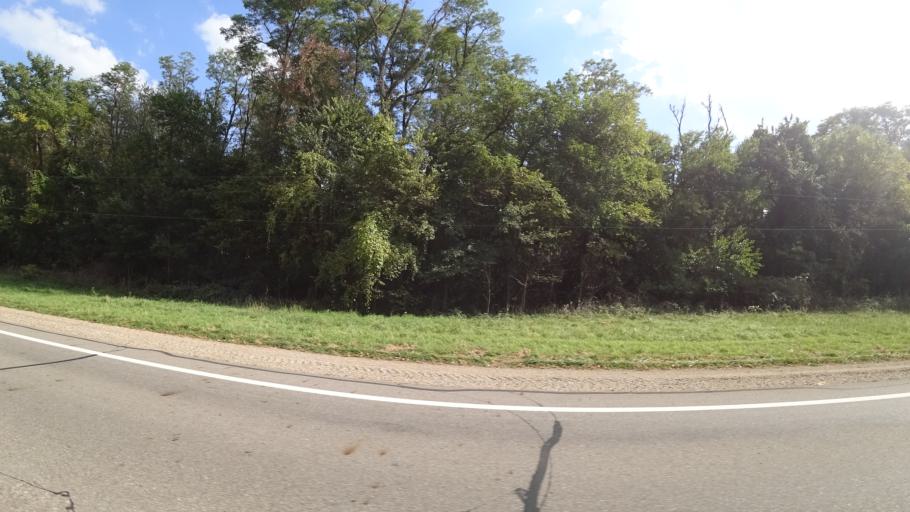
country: US
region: Michigan
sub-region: Saint Joseph County
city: Three Rivers
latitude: 41.9618
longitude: -85.5765
